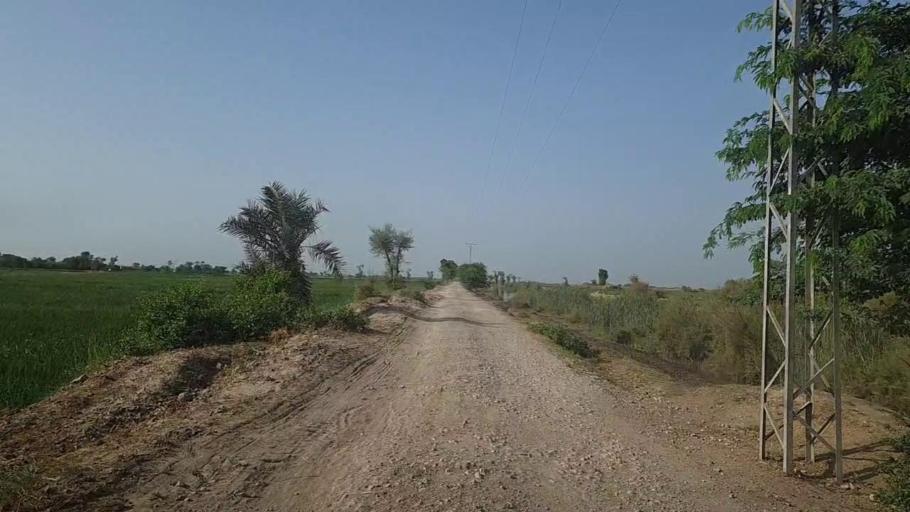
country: PK
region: Sindh
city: Sita Road
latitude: 27.1054
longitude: 67.8746
